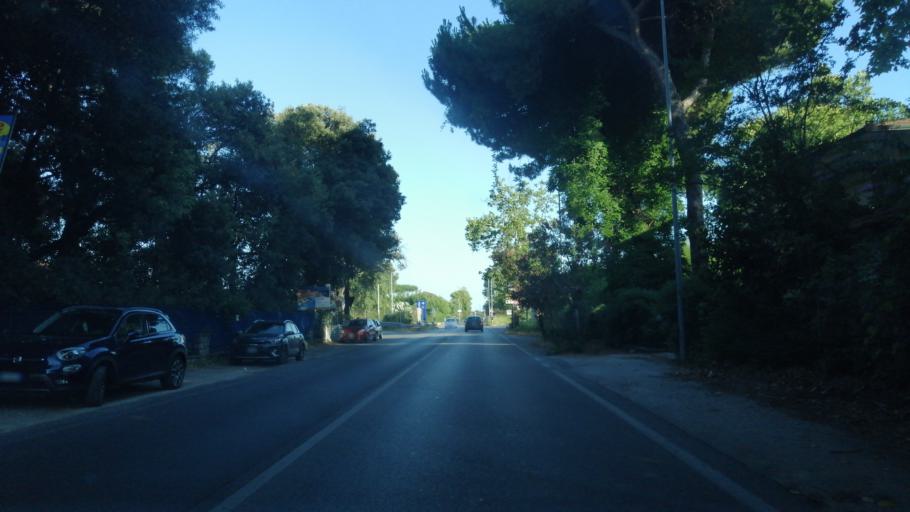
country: IT
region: Tuscany
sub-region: Provincia di Lucca
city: Camaiore
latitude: 43.9130
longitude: 10.2227
